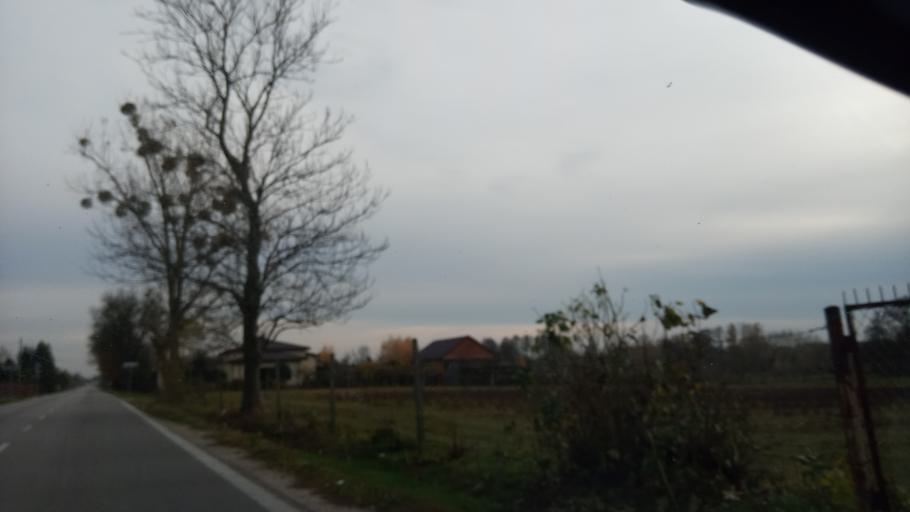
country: PL
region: Lodz Voivodeship
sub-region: Powiat skierniewicki
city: Bolimow
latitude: 52.1616
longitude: 20.1794
